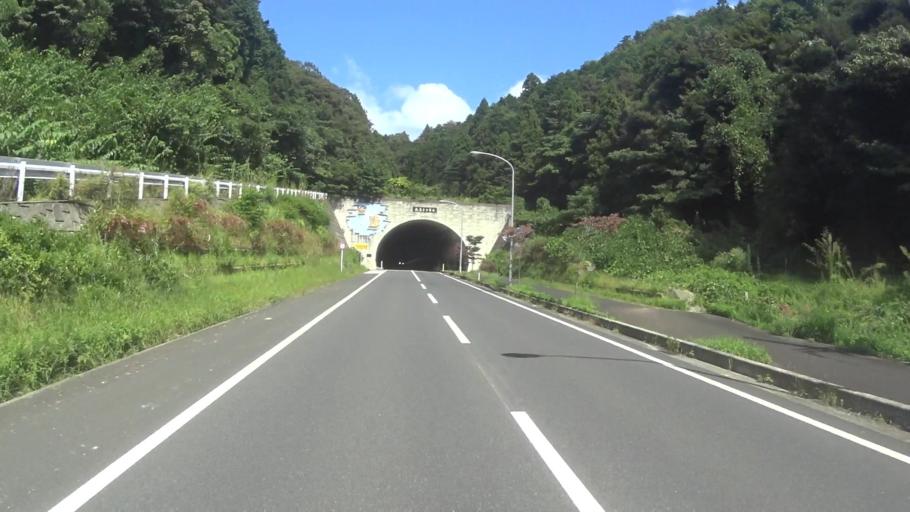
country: JP
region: Kyoto
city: Miyazu
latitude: 35.6691
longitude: 135.2682
